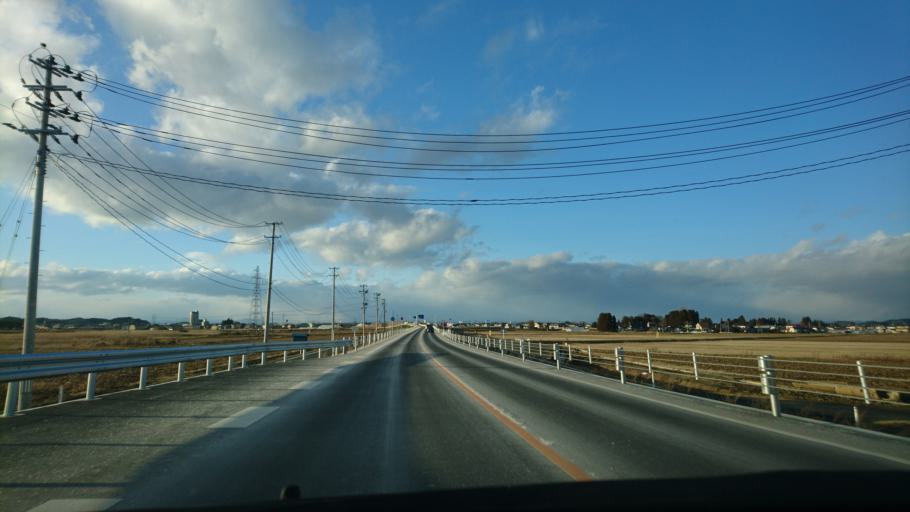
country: JP
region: Miyagi
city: Wakuya
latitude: 38.6904
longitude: 141.2196
